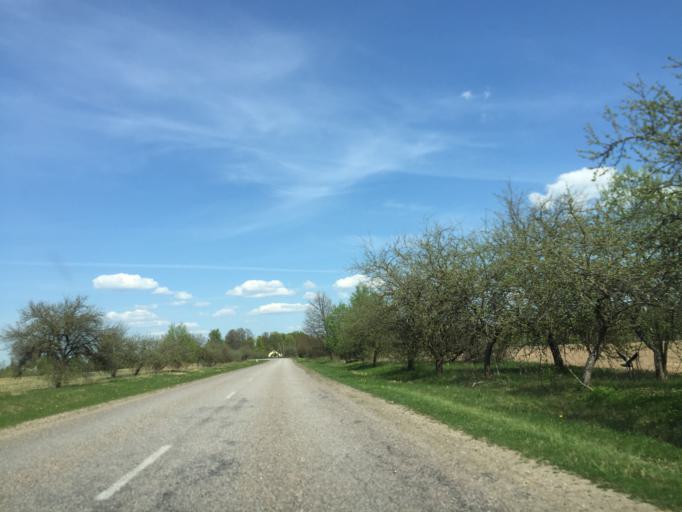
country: LV
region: Krimulda
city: Ragana
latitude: 57.3184
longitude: 24.6419
